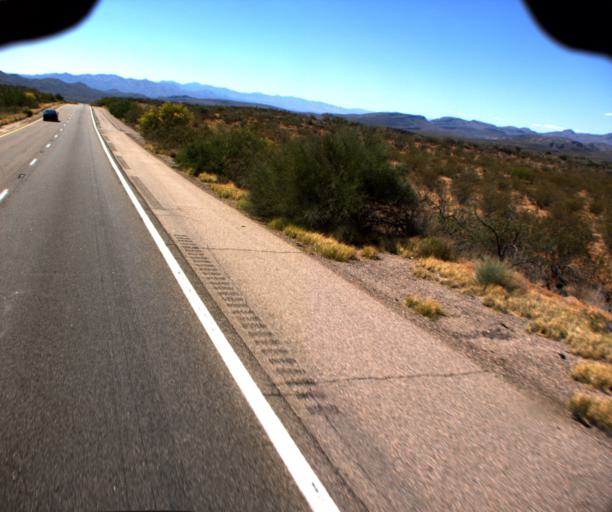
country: US
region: Arizona
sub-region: Yavapai County
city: Bagdad
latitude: 34.4889
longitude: -113.3793
